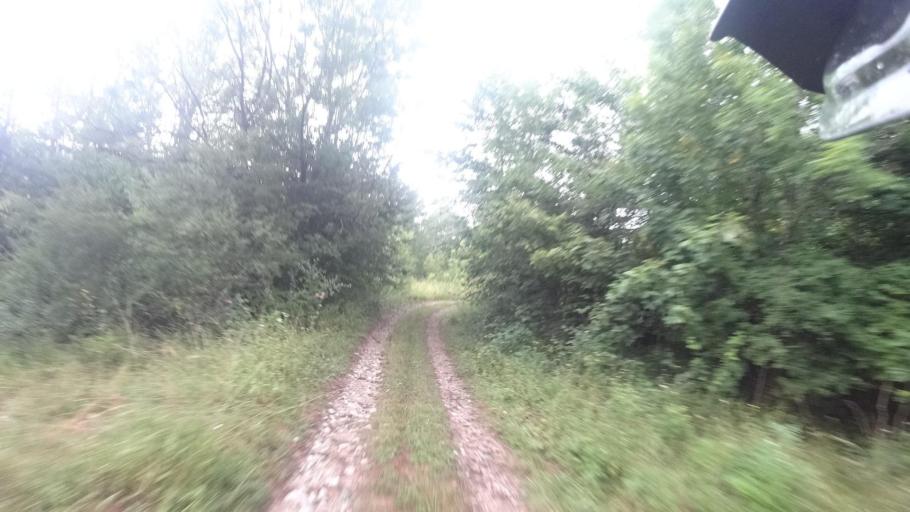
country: HR
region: Licko-Senjska
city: Jezerce
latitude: 44.8124
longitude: 15.6276
